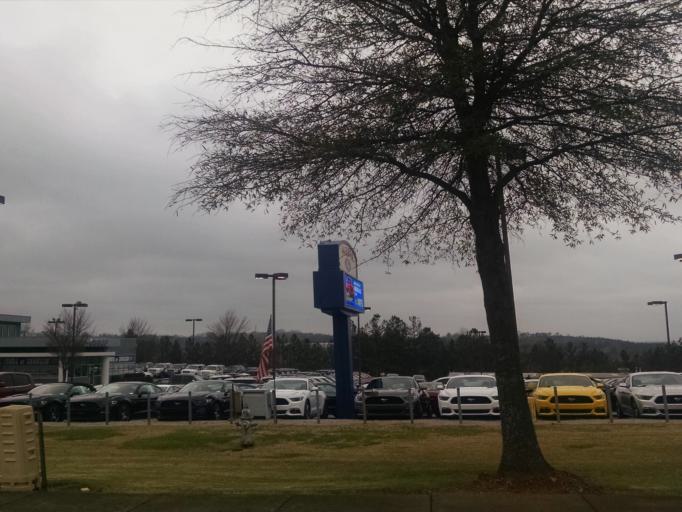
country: US
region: Georgia
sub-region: Gwinnett County
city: Sugar Hill
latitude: 34.0993
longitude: -84.0175
